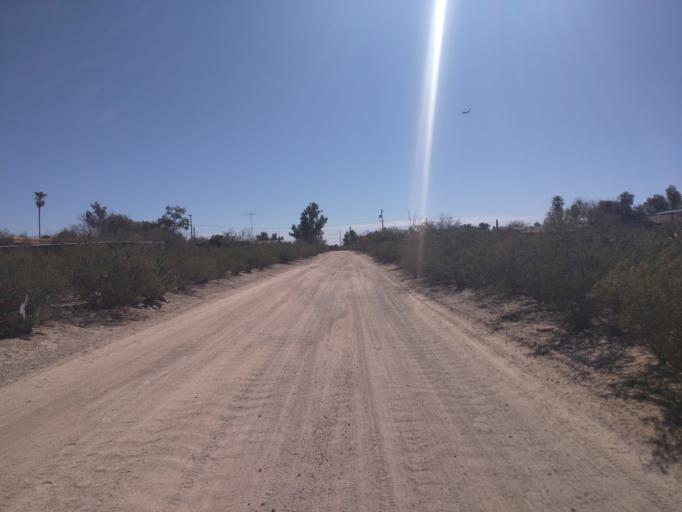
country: US
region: Arizona
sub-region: Pima County
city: Catalina Foothills
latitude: 32.2699
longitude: -110.9502
